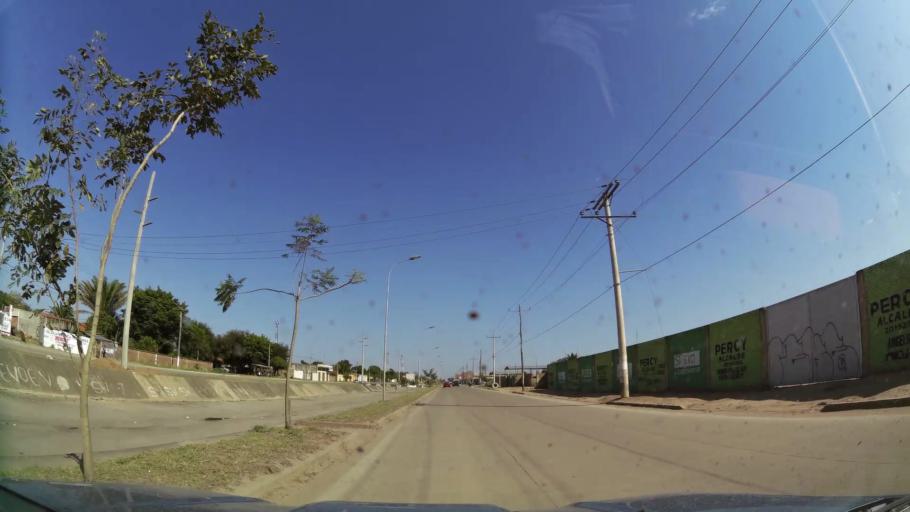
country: BO
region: Santa Cruz
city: Cotoca
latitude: -17.7886
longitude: -63.1084
